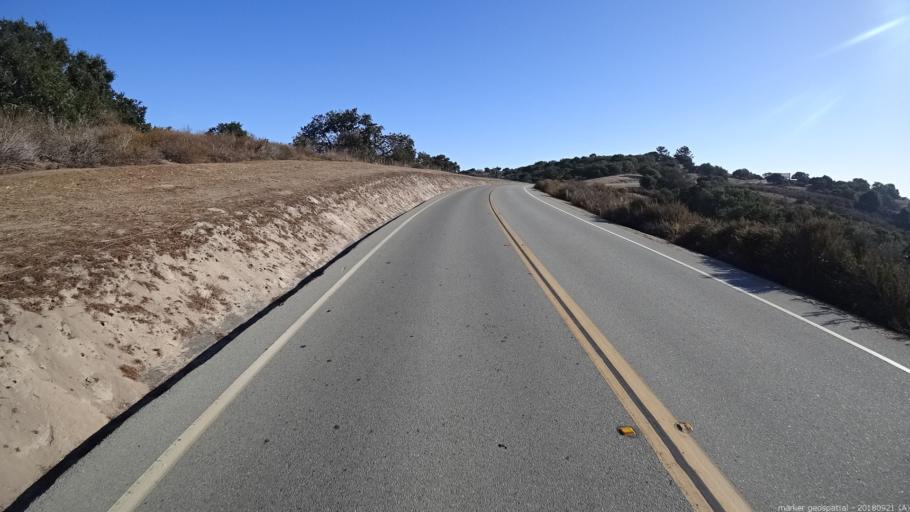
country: US
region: California
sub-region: Monterey County
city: Carmel Valley Village
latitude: 36.5763
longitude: -121.7603
